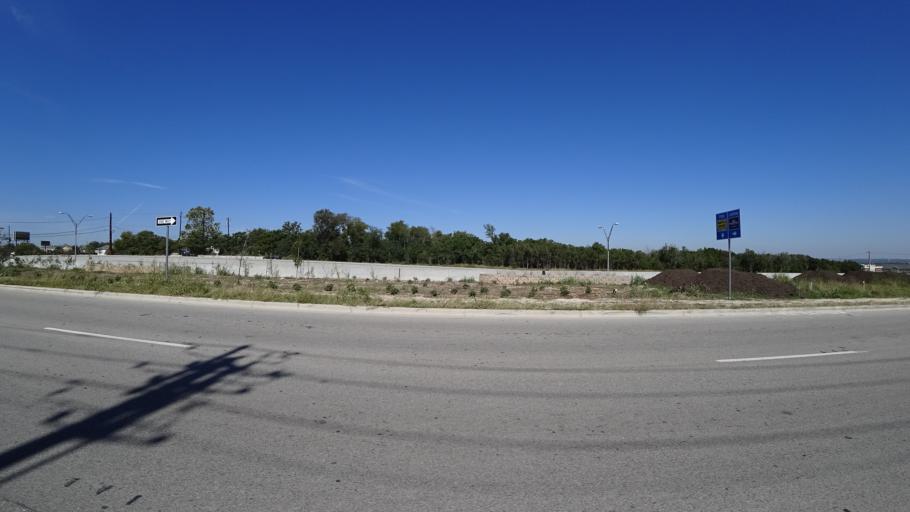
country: US
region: Texas
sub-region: Travis County
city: Austin
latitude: 30.2171
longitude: -97.6933
